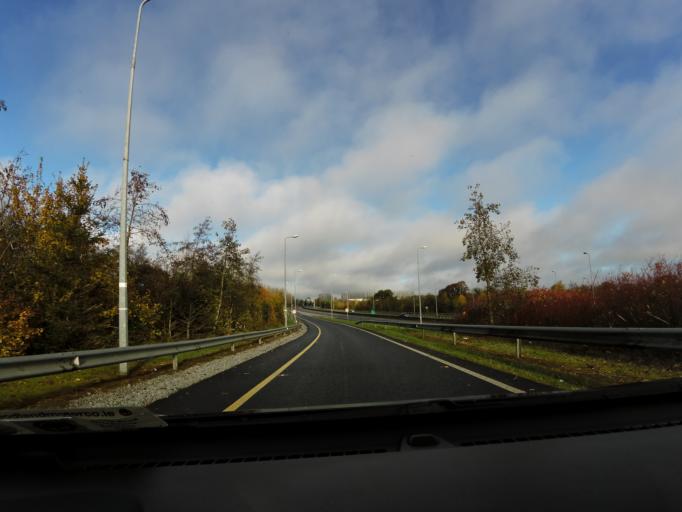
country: IE
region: Leinster
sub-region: An Iarmhi
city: Athlone
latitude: 53.4159
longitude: -7.8900
